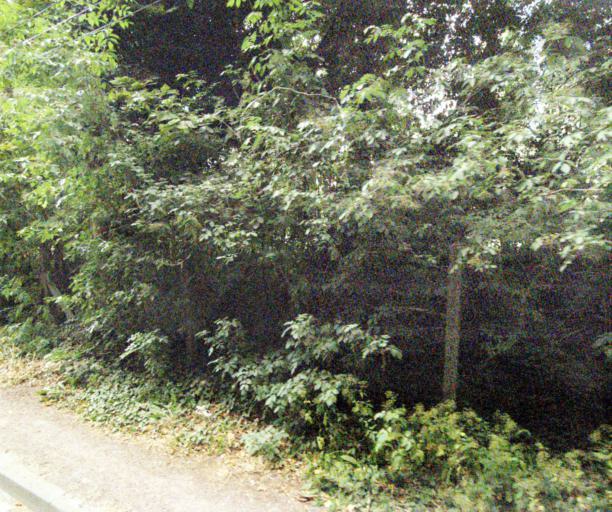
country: FR
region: Nord-Pas-de-Calais
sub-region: Departement du Nord
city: Mouvaux
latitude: 50.7145
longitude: 3.1190
